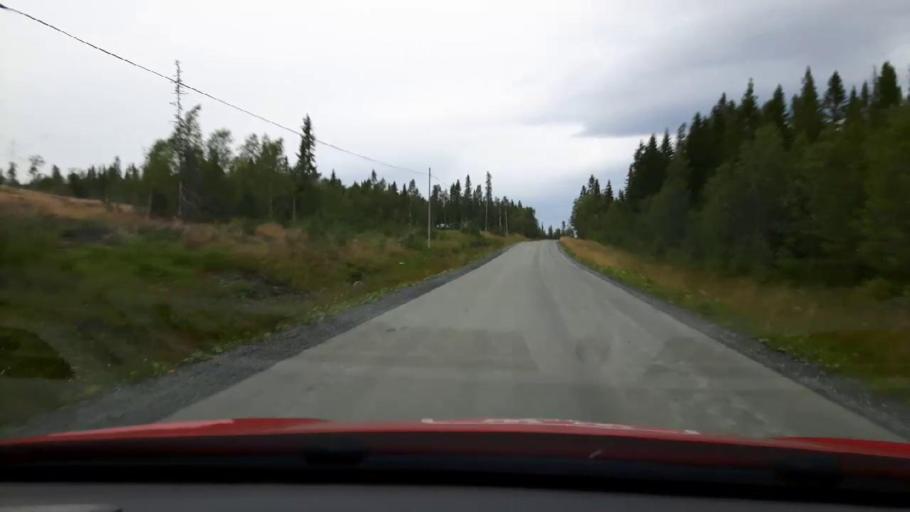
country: SE
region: Jaemtland
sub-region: Are Kommun
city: Are
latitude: 63.4812
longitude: 13.1511
